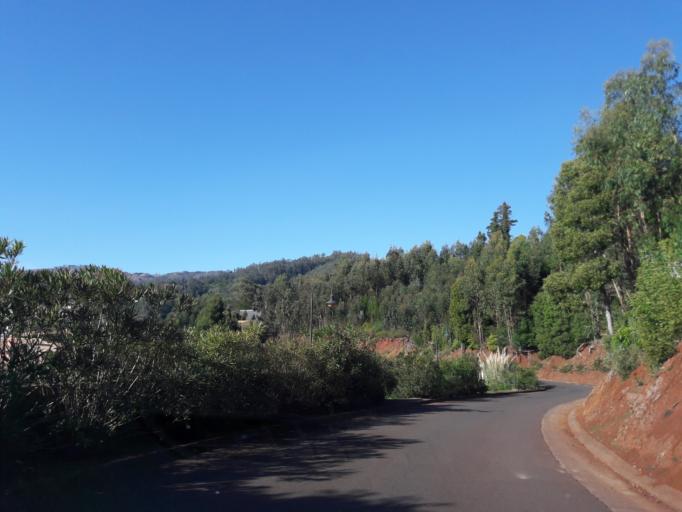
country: PT
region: Madeira
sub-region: Funchal
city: Nossa Senhora do Monte
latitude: 32.6554
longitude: -16.8720
